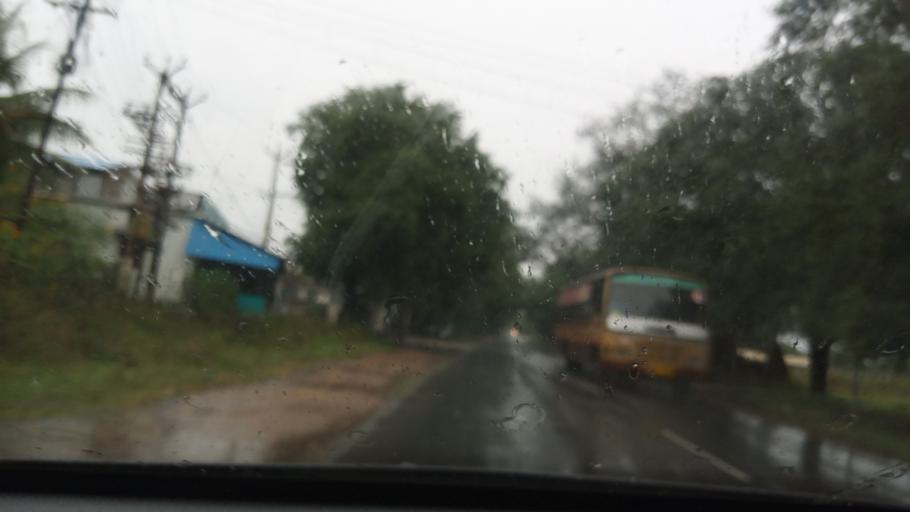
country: IN
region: Tamil Nadu
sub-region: Vellore
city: Walajapet
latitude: 12.8489
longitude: 79.3909
